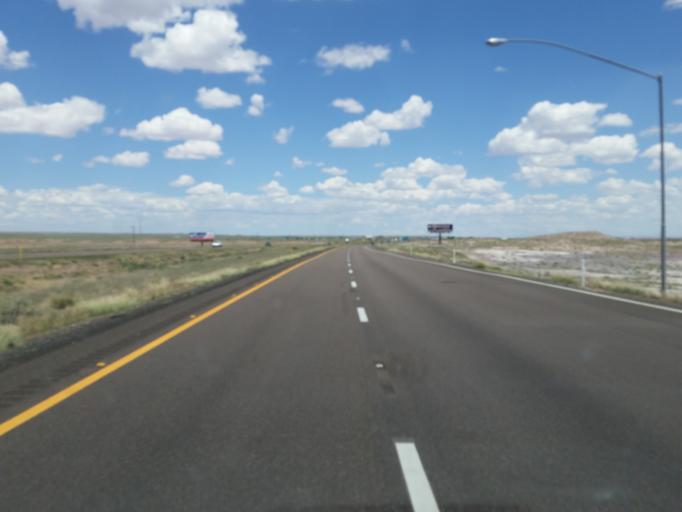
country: US
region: Arizona
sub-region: Navajo County
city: Holbrook
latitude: 34.9754
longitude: -110.0808
